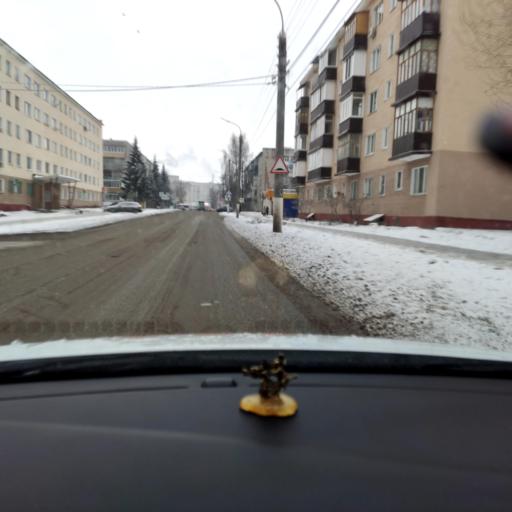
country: RU
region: Tatarstan
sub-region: Zelenodol'skiy Rayon
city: Zelenodolsk
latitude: 55.8502
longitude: 48.5251
